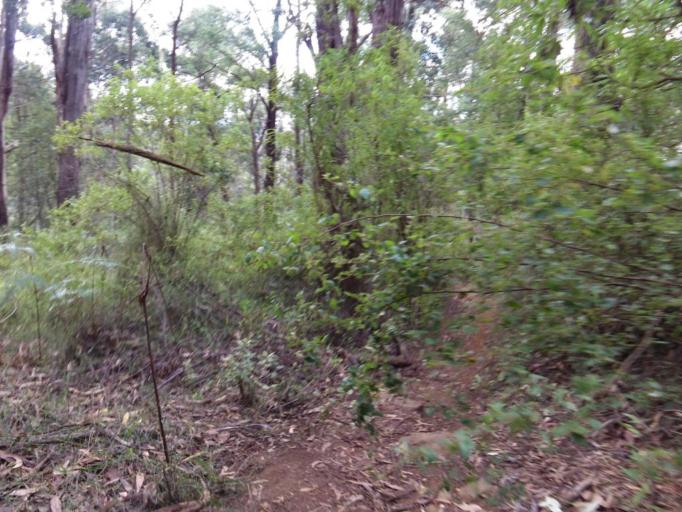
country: AU
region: Victoria
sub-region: Yarra Ranges
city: Olinda
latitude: -37.8436
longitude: 145.3772
